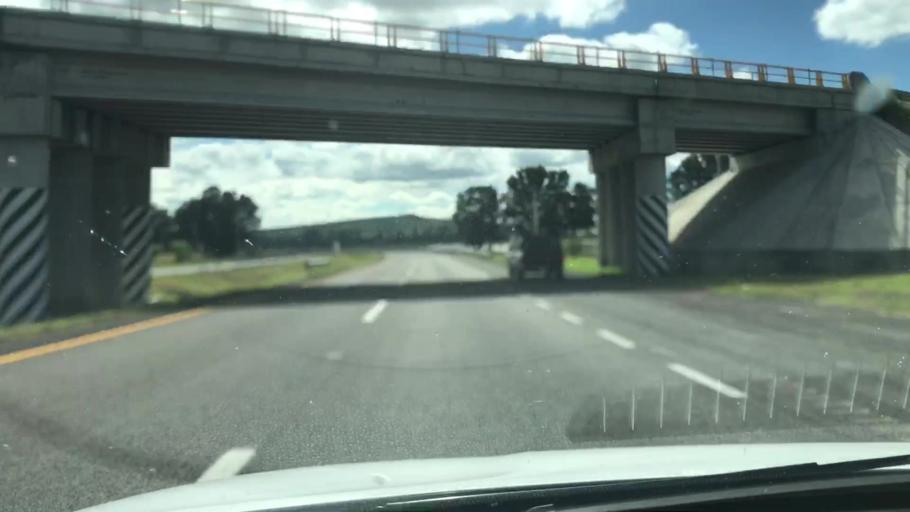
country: MX
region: Guanajuato
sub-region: Irapuato
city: Serrano
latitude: 20.7665
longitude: -101.3929
